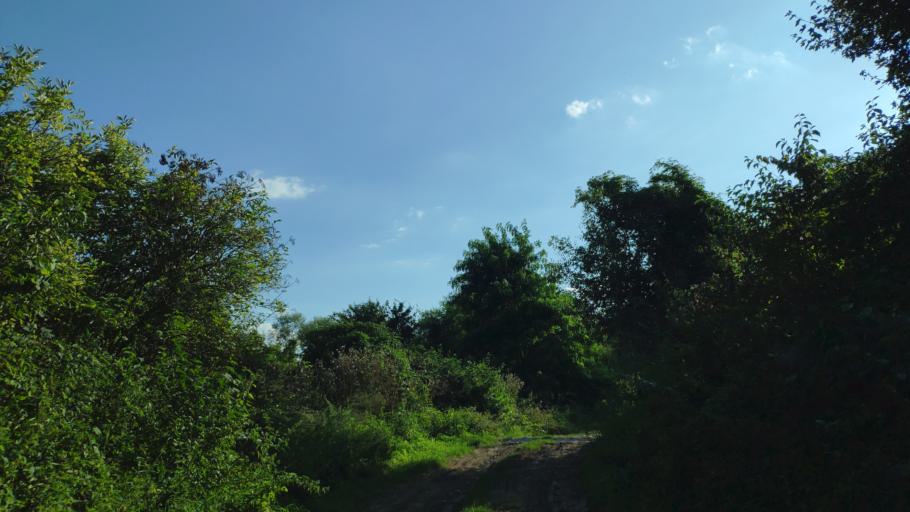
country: SK
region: Kosicky
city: Secovce
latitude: 48.6118
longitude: 21.5378
